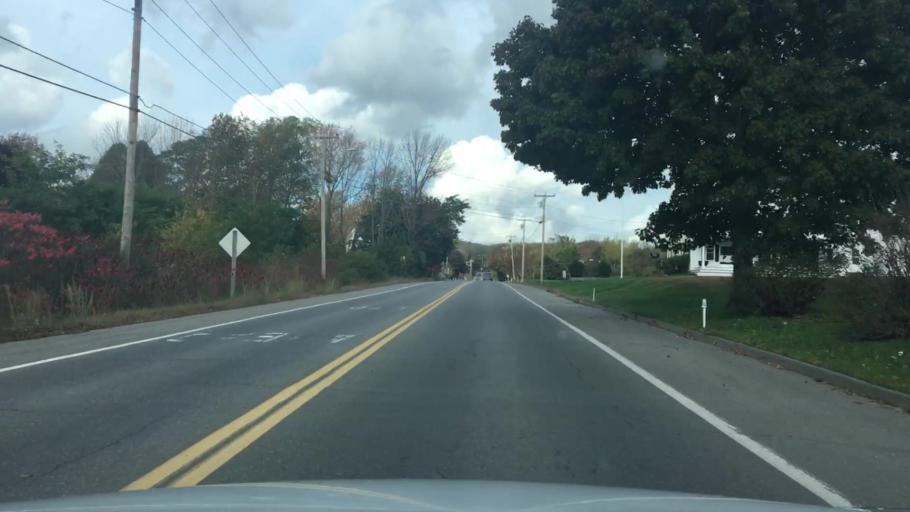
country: US
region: Maine
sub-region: Knox County
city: Rockland
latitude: 44.1189
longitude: -69.1104
